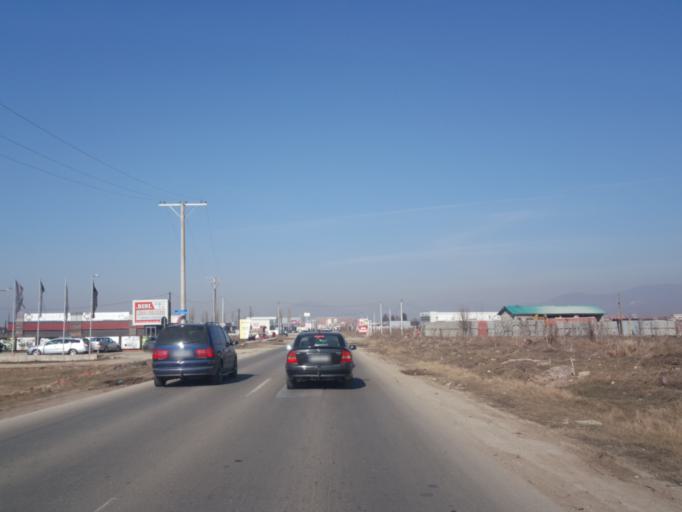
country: XK
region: Mitrovica
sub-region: Vushtrri
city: Vushtrri
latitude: 42.8054
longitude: 20.9910
